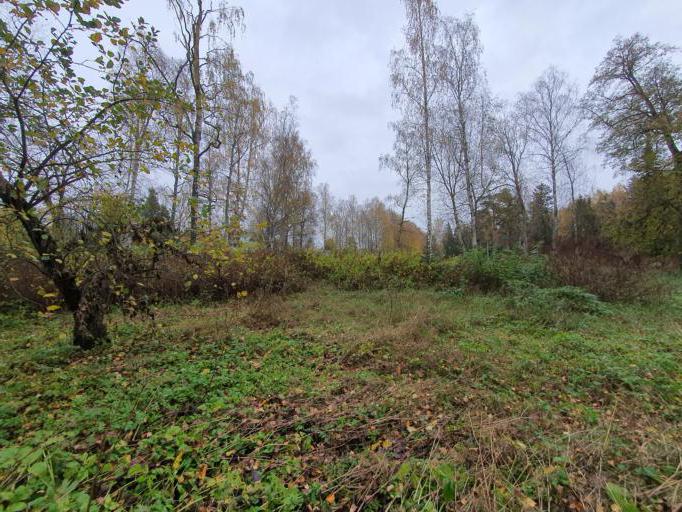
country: RU
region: St.-Petersburg
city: Tyarlevo
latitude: 59.6981
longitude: 30.4561
